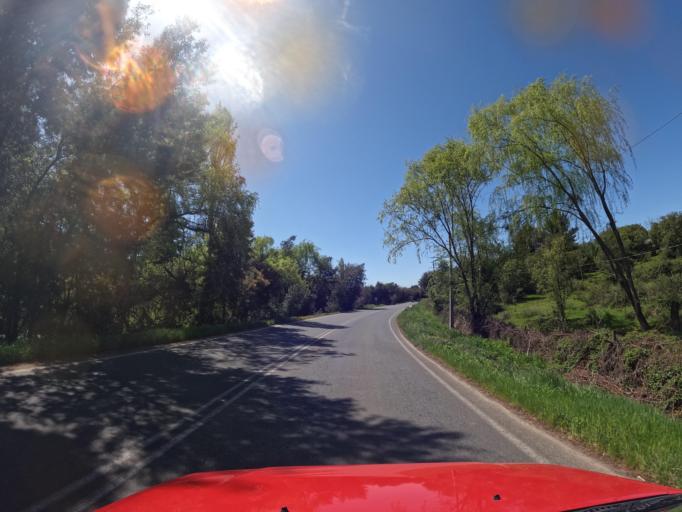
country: CL
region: Maule
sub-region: Provincia de Talca
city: San Clemente
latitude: -35.4828
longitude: -71.2713
